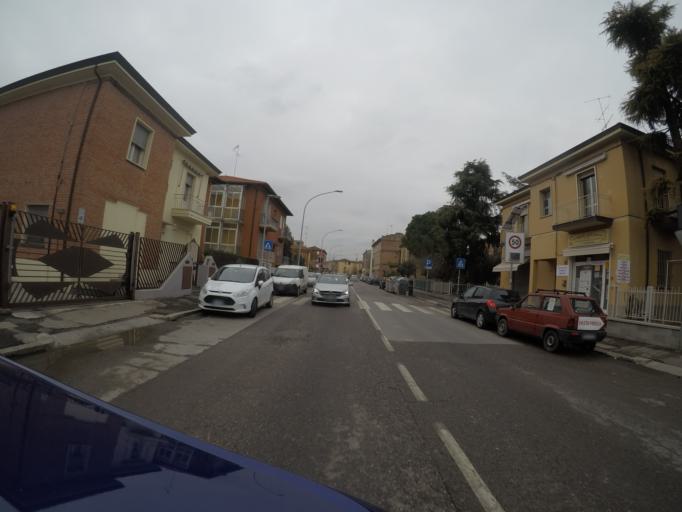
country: IT
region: Emilia-Romagna
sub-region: Provincia di Bologna
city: Trebbo
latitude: 44.5221
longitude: 11.2955
